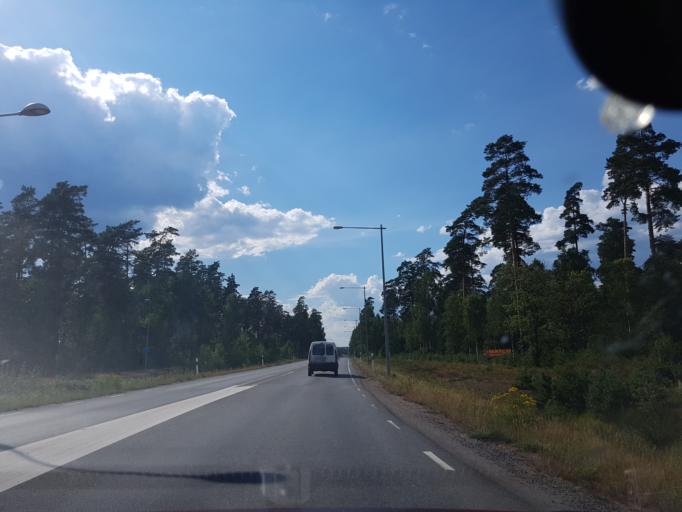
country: SE
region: Joenkoeping
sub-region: Gislaveds Kommun
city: Gislaved
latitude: 57.2941
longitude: 13.5762
